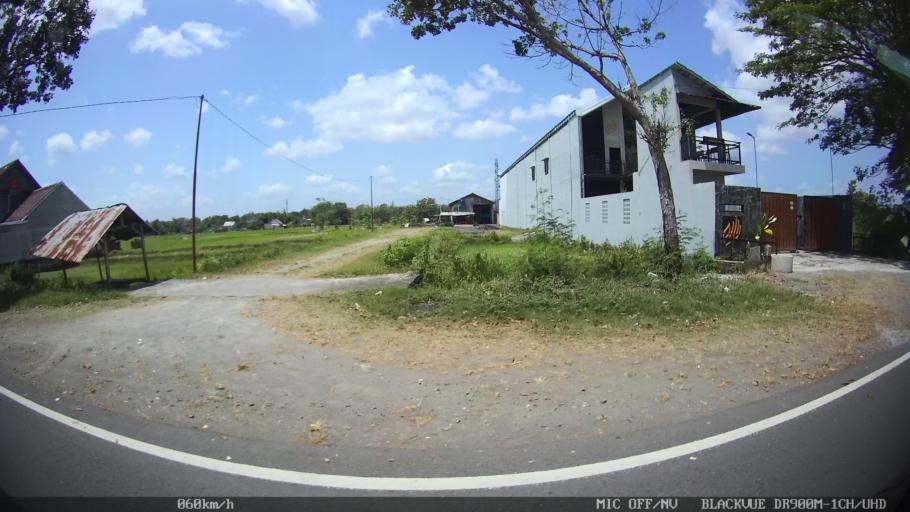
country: ID
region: Daerah Istimewa Yogyakarta
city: Bantul
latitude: -7.8923
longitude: 110.3471
